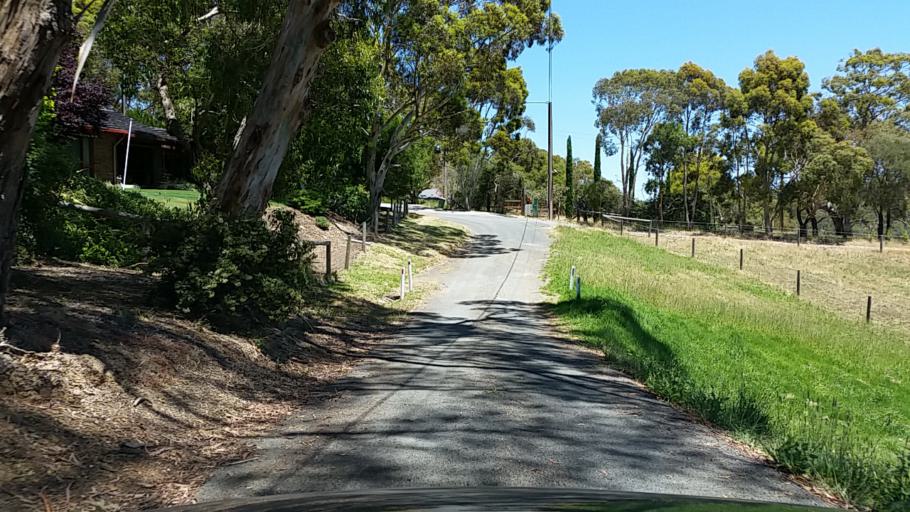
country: AU
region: South Australia
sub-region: Burnside
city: Mount Osmond
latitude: -34.9890
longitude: 138.6714
